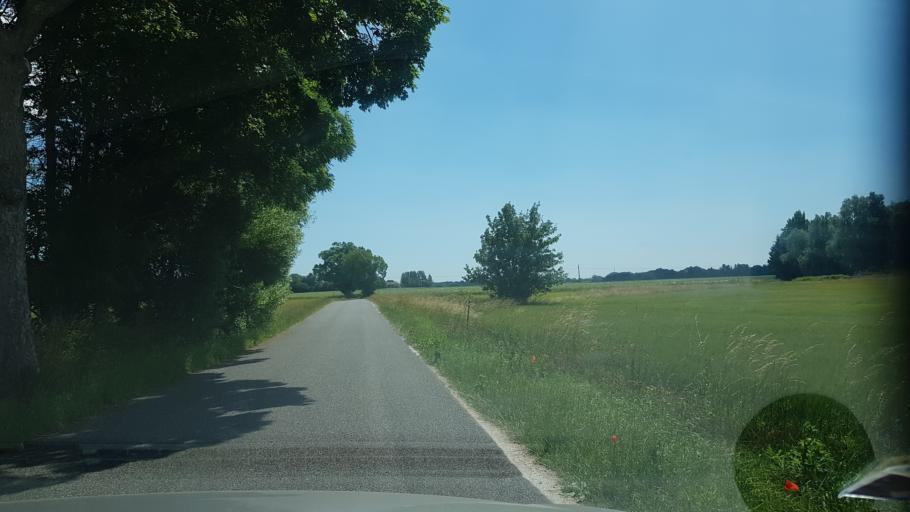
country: DK
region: Zealand
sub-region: Kalundborg Kommune
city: Svebolle
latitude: 55.7034
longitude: 11.2868
